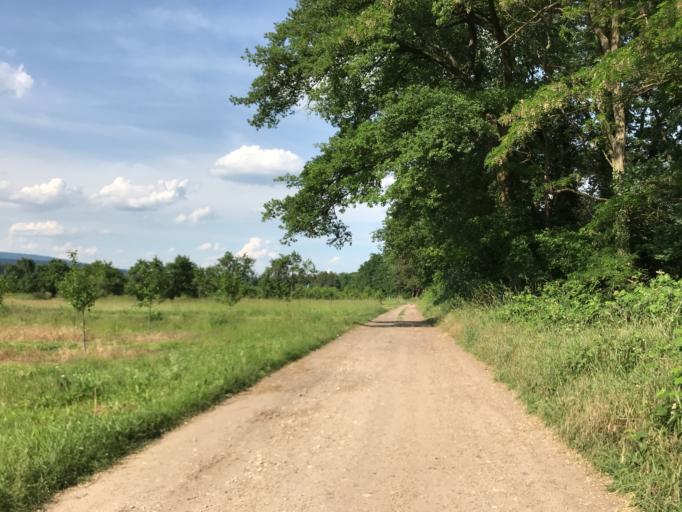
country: DE
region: Hesse
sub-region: Regierungsbezirk Darmstadt
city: Eltville
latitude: 50.0080
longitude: 8.1329
